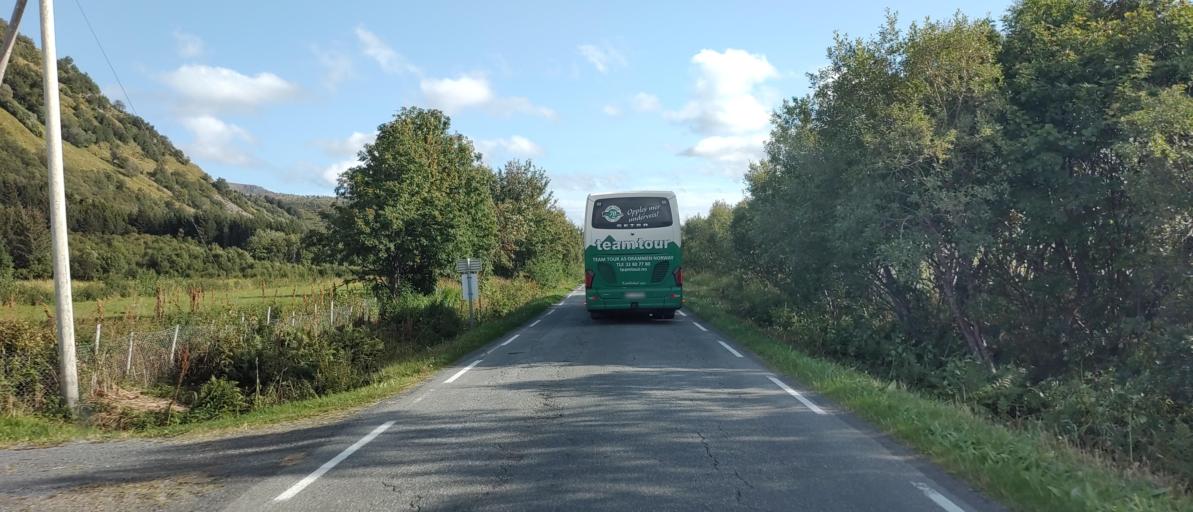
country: NO
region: Nordland
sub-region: Sortland
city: Sortland
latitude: 69.0352
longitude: 15.5244
